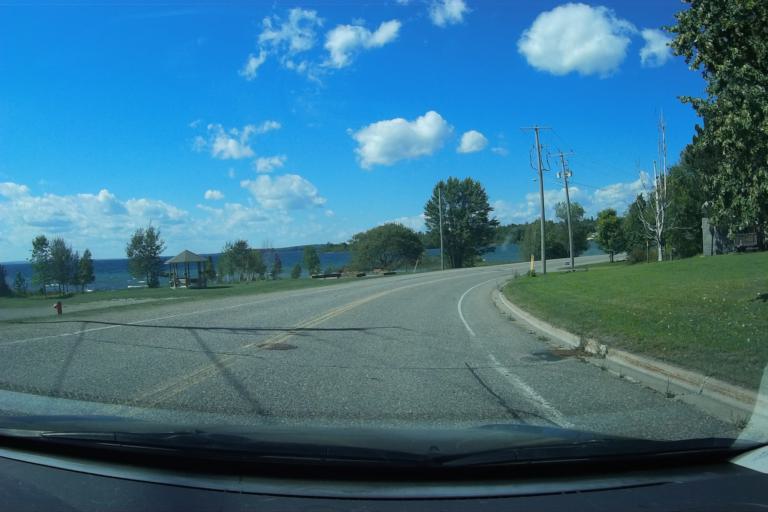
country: CA
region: Ontario
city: Thessalon
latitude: 46.2572
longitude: -83.5639
